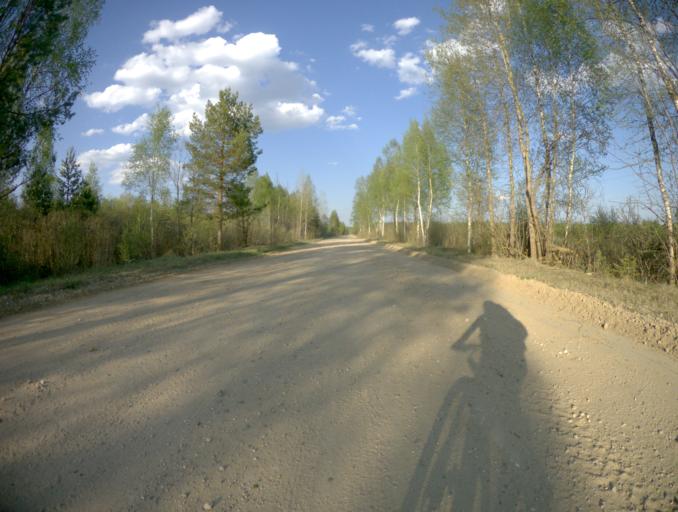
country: RU
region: Ivanovo
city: Yuzha
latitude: 56.5522
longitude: 41.8116
